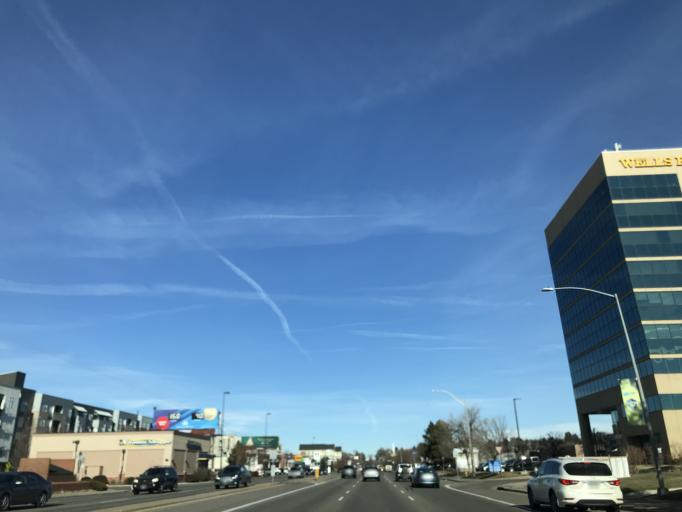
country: US
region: Colorado
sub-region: Arapahoe County
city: Glendale
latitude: 39.7087
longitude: -104.9406
